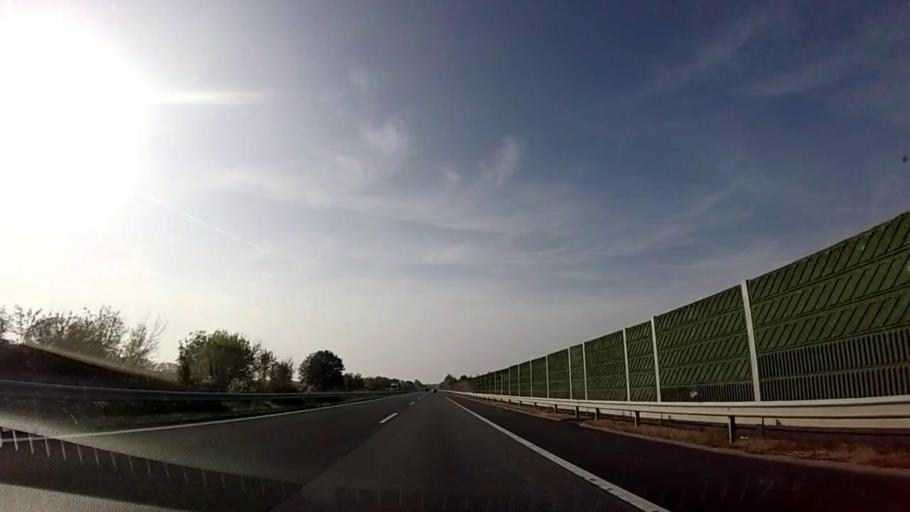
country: HU
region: Somogy
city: Balatonszabadi
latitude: 46.9482
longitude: 18.1500
